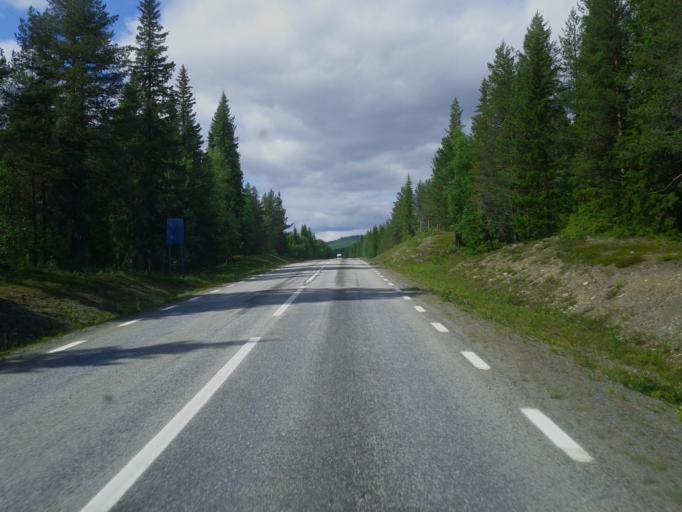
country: SE
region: Vaesterbotten
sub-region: Storumans Kommun
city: Fristad
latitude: 65.3871
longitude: 16.4792
